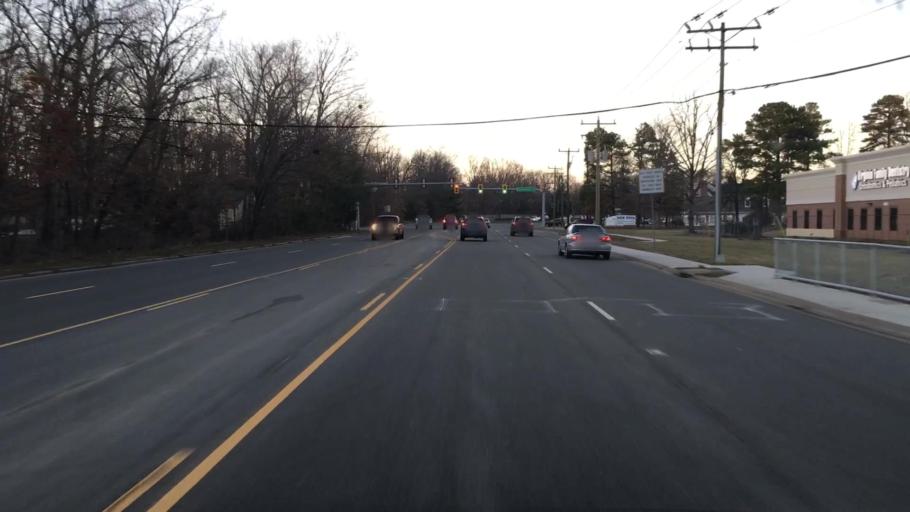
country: US
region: Virginia
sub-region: Chesterfield County
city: Bon Air
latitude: 37.5166
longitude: -77.6156
